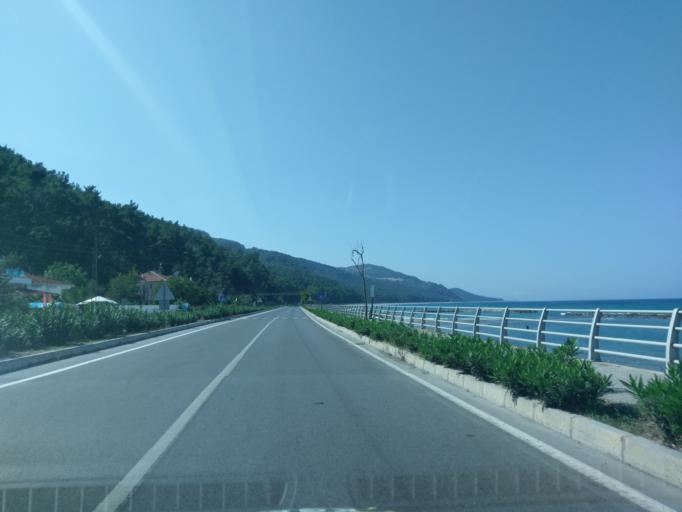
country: TR
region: Samsun
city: Yakakent
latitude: 41.6451
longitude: 35.4765
